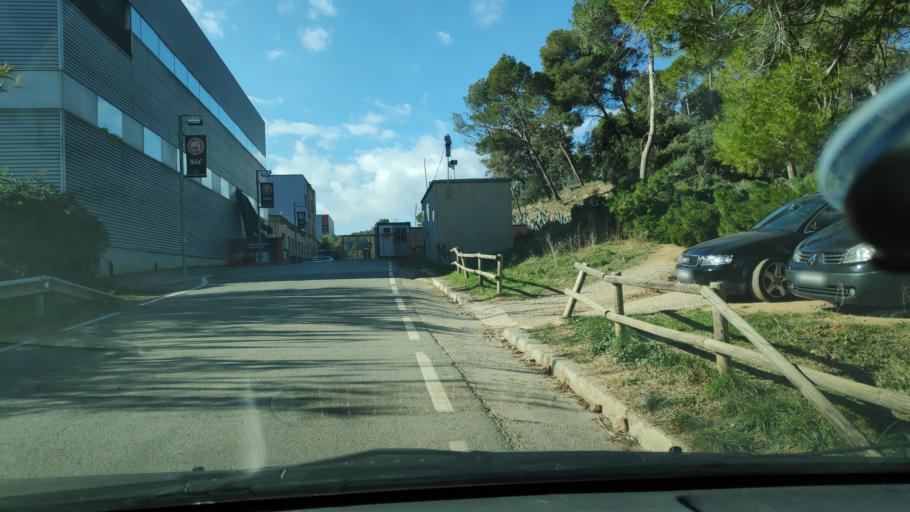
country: ES
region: Catalonia
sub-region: Provincia de Barcelona
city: Matadepera
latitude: 41.5946
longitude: 2.0081
